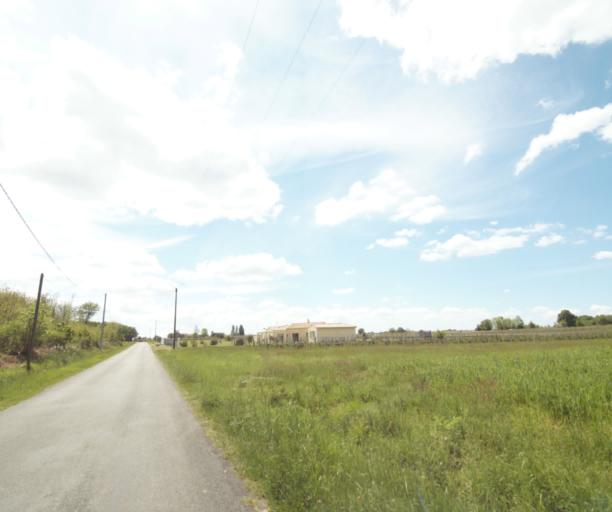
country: FR
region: Poitou-Charentes
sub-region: Departement de la Charente-Maritime
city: Burie
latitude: 45.7534
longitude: -0.4439
